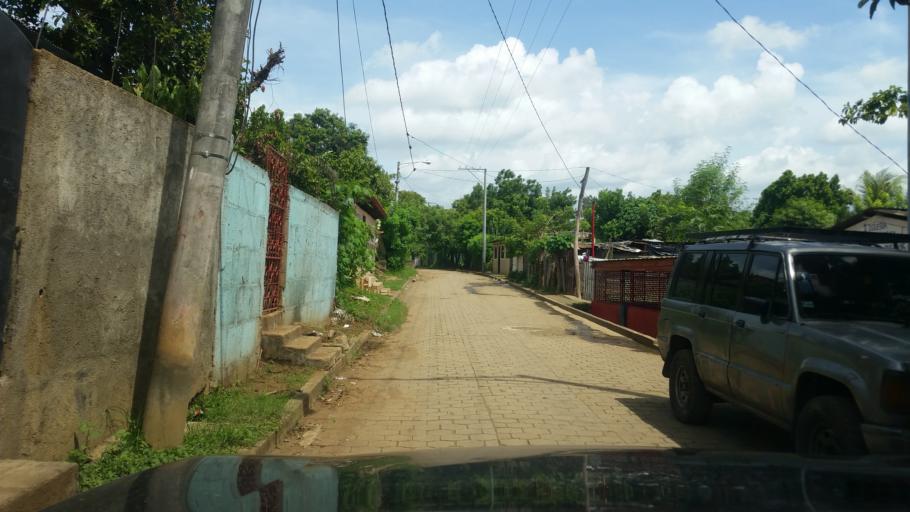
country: NI
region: Managua
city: Managua
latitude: 12.1055
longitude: -86.2397
